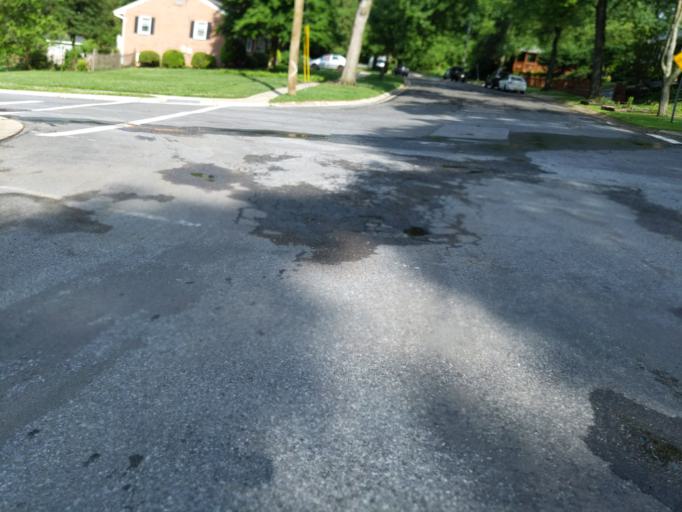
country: US
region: Maryland
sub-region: Montgomery County
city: Kemp Mill
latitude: 39.0321
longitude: -77.0372
